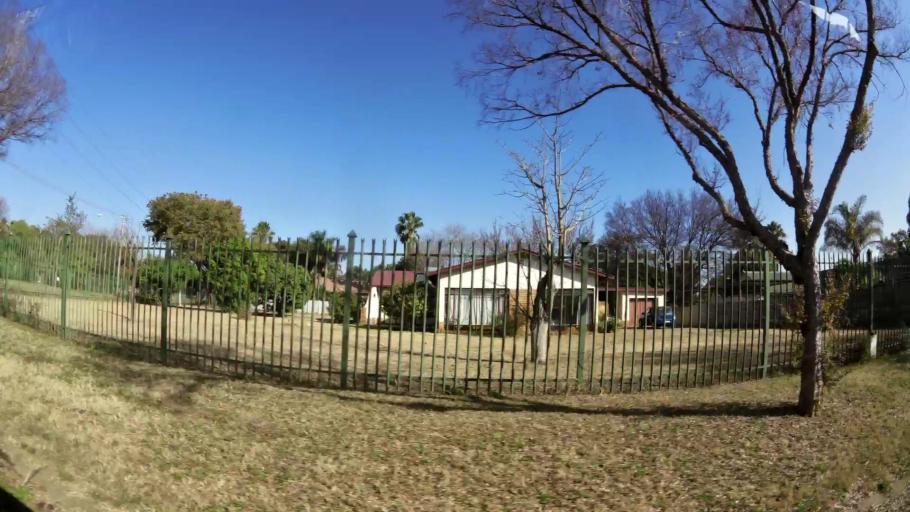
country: ZA
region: Gauteng
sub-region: City of Tshwane Metropolitan Municipality
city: Pretoria
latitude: -25.7259
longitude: 28.2663
